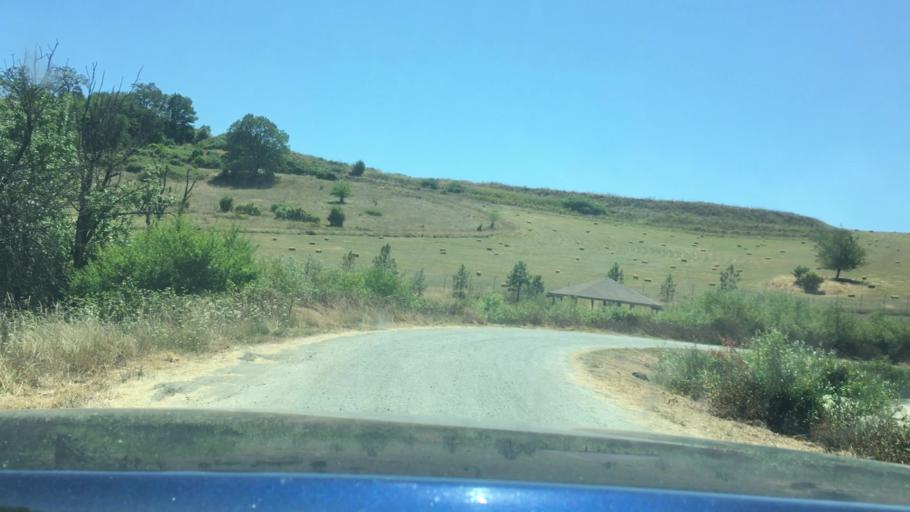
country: US
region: Oregon
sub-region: Douglas County
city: Winston
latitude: 43.1296
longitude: -123.4334
